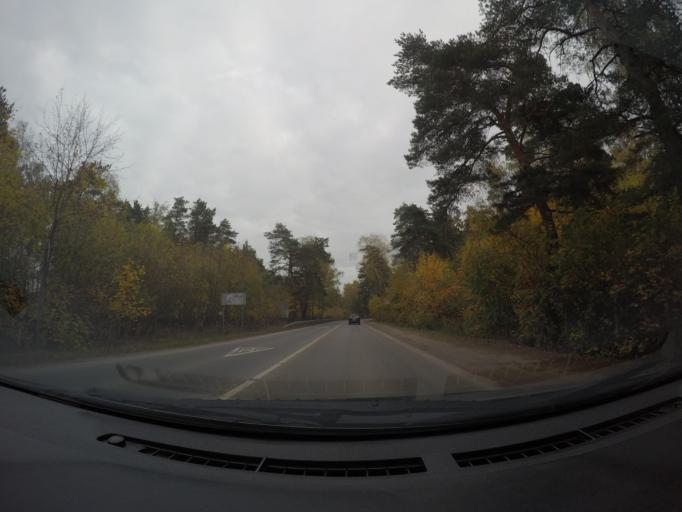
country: RU
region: Moskovskaya
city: Elektrougli
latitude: 55.7696
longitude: 38.2255
